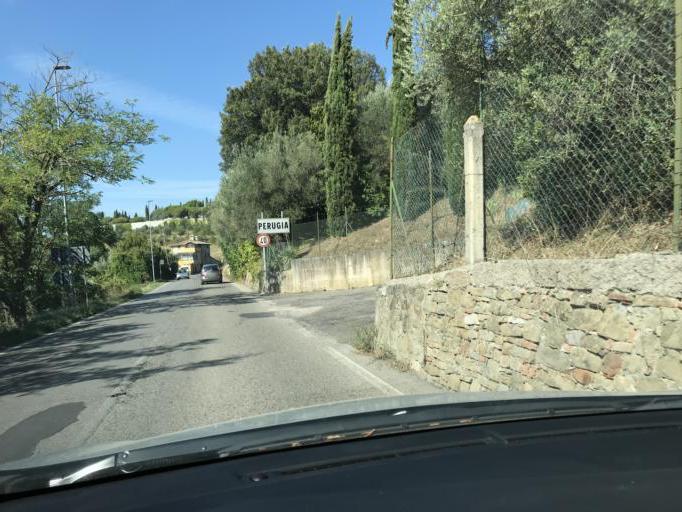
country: IT
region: Umbria
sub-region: Provincia di Perugia
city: Ponte Felcino
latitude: 43.1095
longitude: 12.4236
